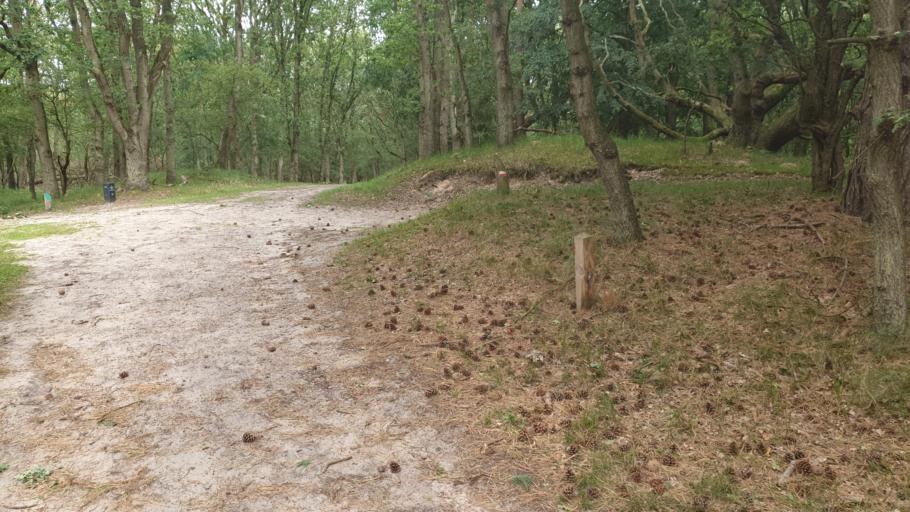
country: NL
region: North Holland
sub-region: Gemeente Zandvoort
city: Zandvoort
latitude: 52.3523
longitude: 4.5660
